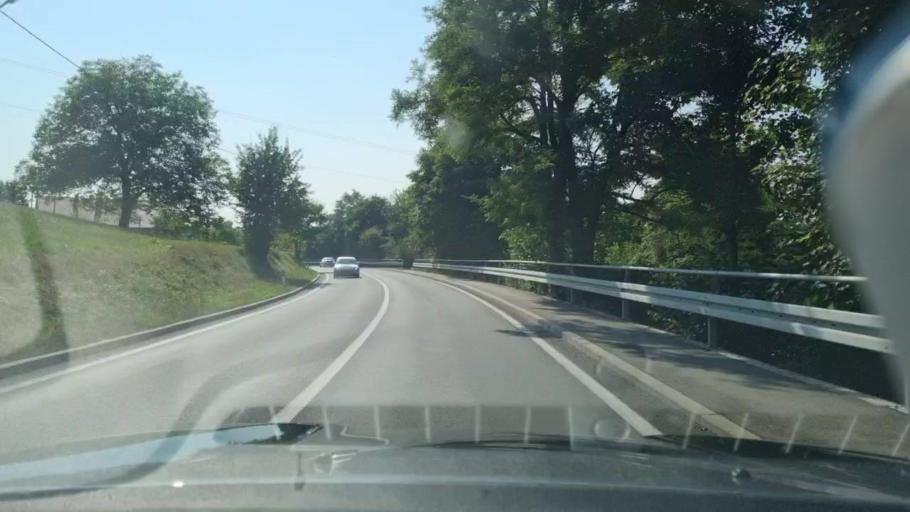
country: BA
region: Federation of Bosnia and Herzegovina
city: Cazin
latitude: 44.9659
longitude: 15.9164
